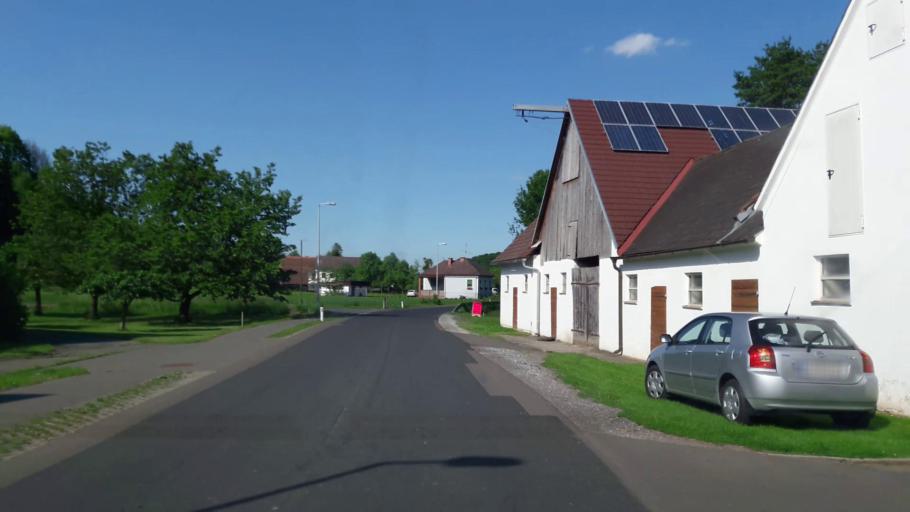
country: AT
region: Styria
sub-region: Politischer Bezirk Suedoststeiermark
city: Fehring
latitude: 46.9185
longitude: 16.0268
